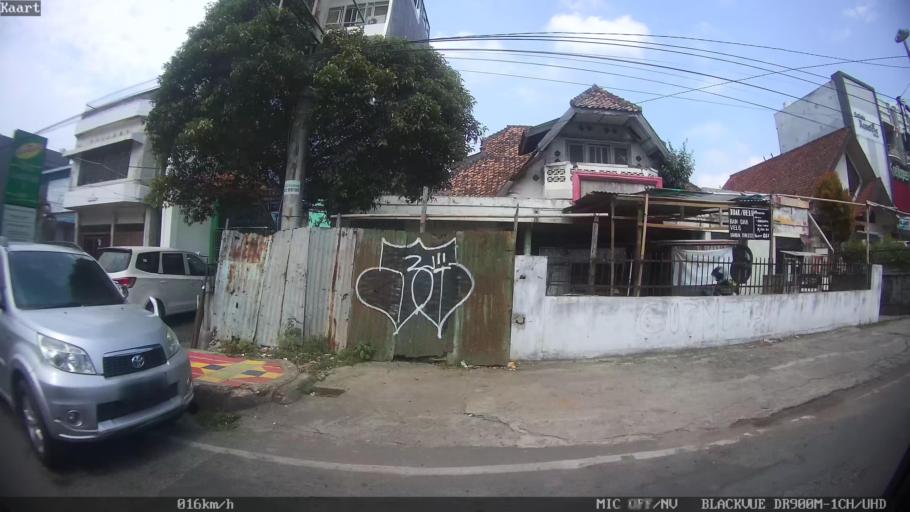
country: ID
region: Lampung
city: Bandarlampung
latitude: -5.4327
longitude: 105.2619
